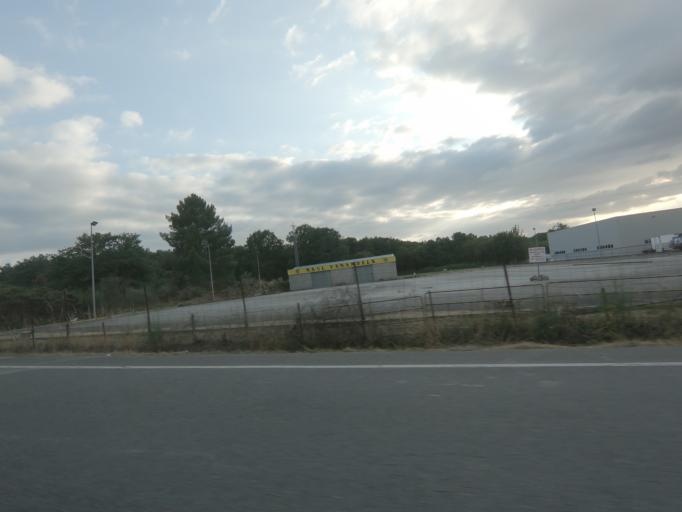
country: ES
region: Galicia
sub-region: Provincia de Ourense
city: Taboadela
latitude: 42.2778
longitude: -7.8363
